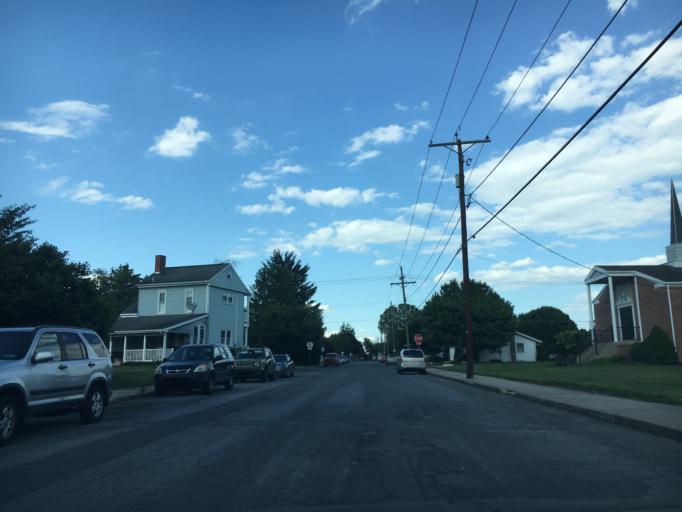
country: US
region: Pennsylvania
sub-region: Berks County
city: Fleetwood
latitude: 40.4539
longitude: -75.8243
